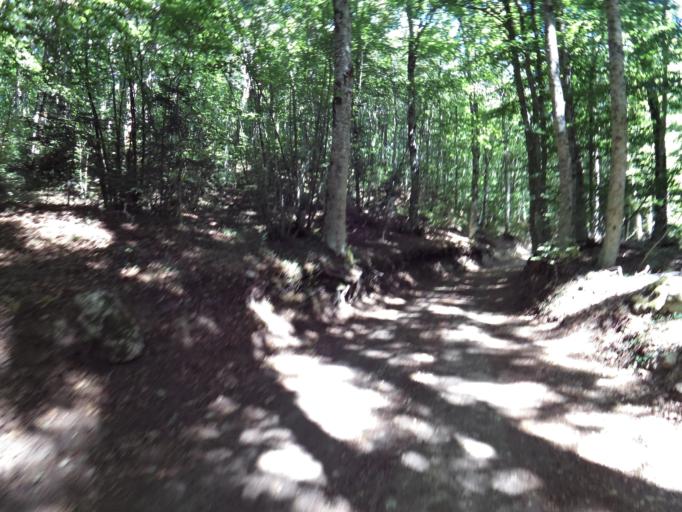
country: IT
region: Calabria
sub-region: Provincia di Vibo-Valentia
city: Mongiana
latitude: 38.5184
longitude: 16.3452
